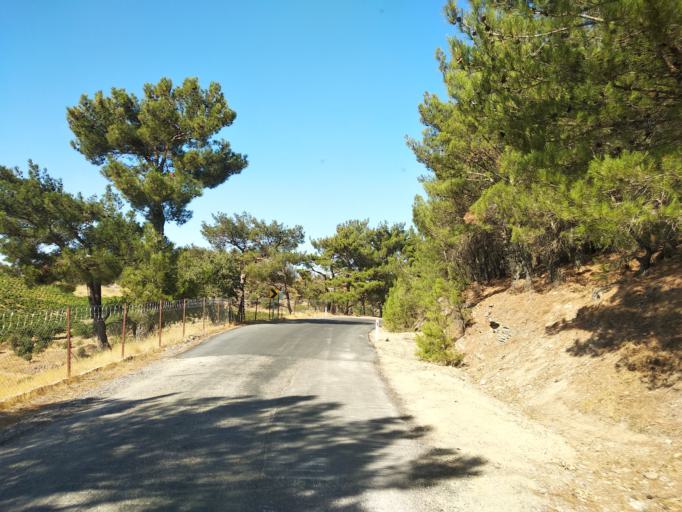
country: TR
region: Izmir
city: Gaziemir
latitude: 38.3042
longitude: 26.9980
